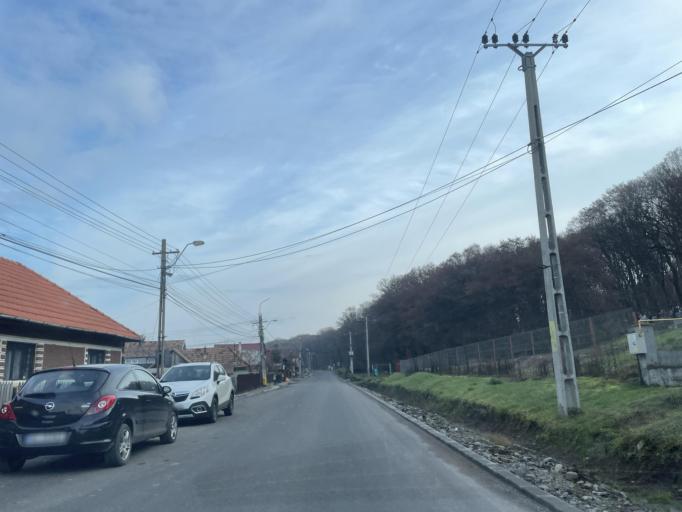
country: RO
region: Mures
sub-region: Comuna Ideciu de Jos
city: Ideciu de Jos
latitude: 46.7762
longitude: 24.7426
